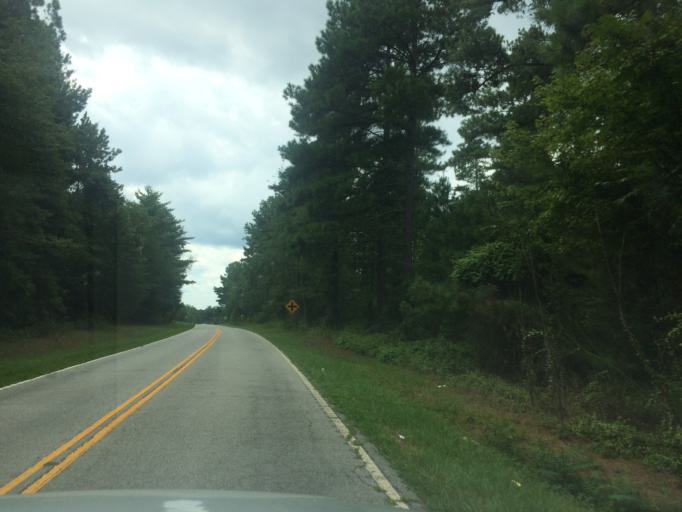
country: US
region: South Carolina
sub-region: Spartanburg County
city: Inman
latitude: 35.1541
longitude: -82.0359
